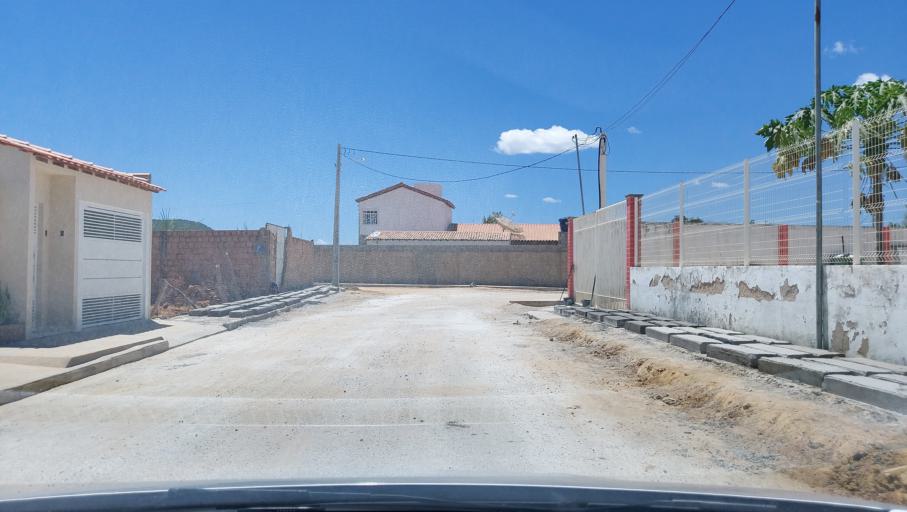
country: BR
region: Bahia
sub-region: Oliveira Dos Brejinhos
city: Beira Rio
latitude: -12.0038
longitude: -42.6300
